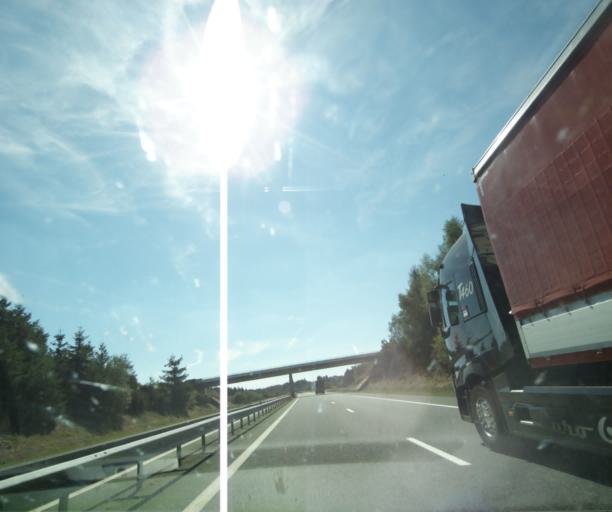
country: FR
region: Limousin
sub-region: Departement de la Correze
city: Ussel
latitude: 45.5437
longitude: 2.3595
